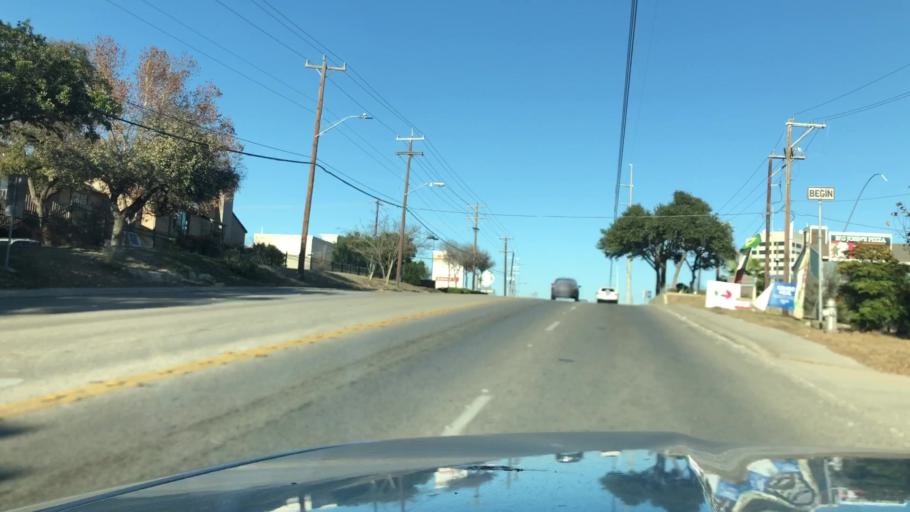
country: US
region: Texas
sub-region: Bexar County
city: Balcones Heights
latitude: 29.5084
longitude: -98.5551
